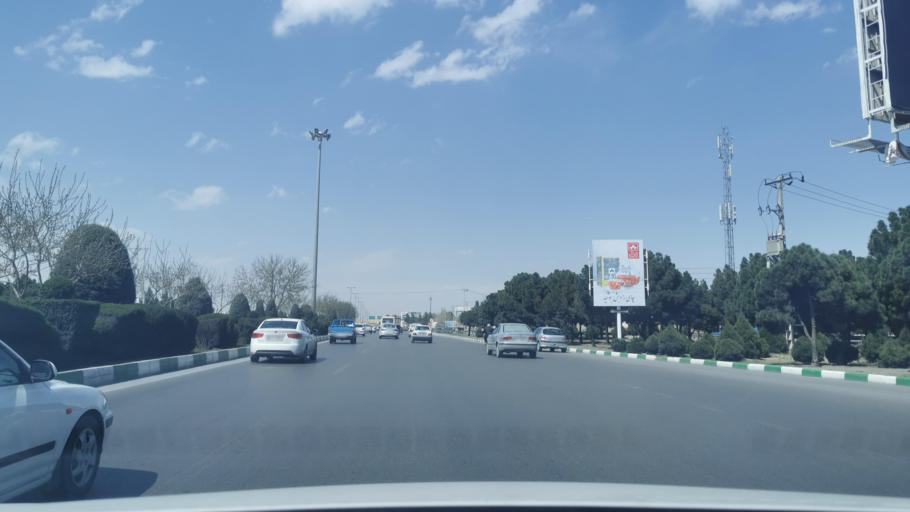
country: IR
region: Razavi Khorasan
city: Mashhad
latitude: 36.3474
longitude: 59.5474
